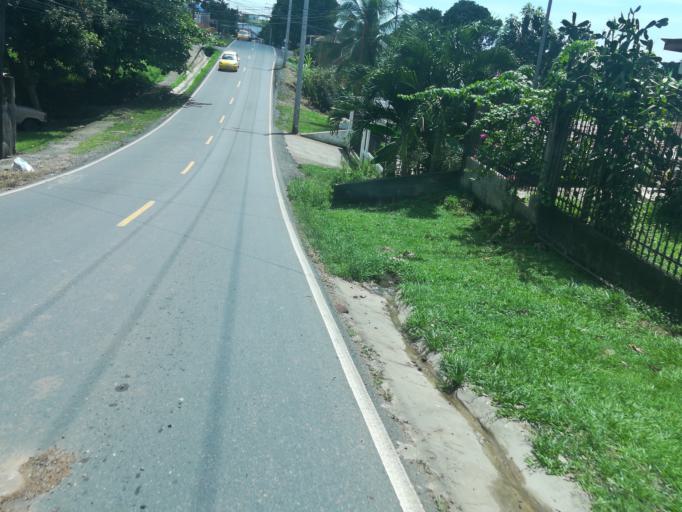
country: PA
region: Panama
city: Tocumen
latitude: 9.0928
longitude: -79.4027
